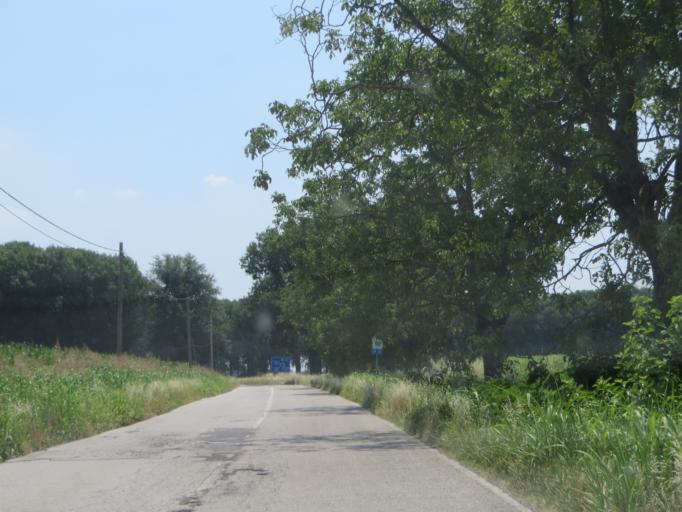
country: IT
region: Veneto
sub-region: Provincia di Verona
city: San Pietro di Morubio
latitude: 45.2319
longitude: 11.2314
